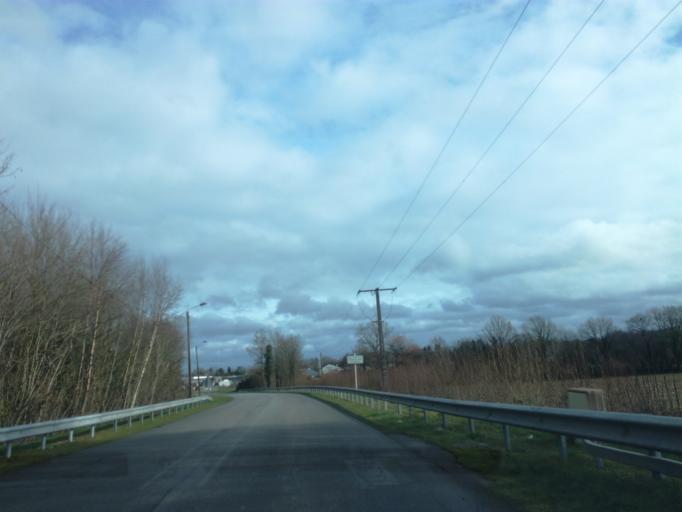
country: FR
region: Brittany
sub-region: Departement du Morbihan
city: Le Sourn
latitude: 48.0370
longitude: -2.9697
